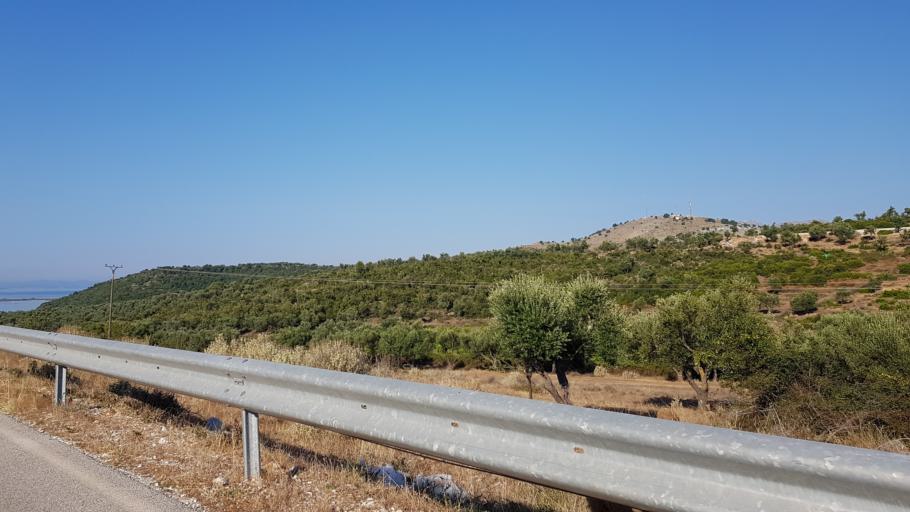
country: AL
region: Vlore
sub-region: Rrethi i Sarandes
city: Xarre
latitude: 39.7590
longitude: 20.0017
